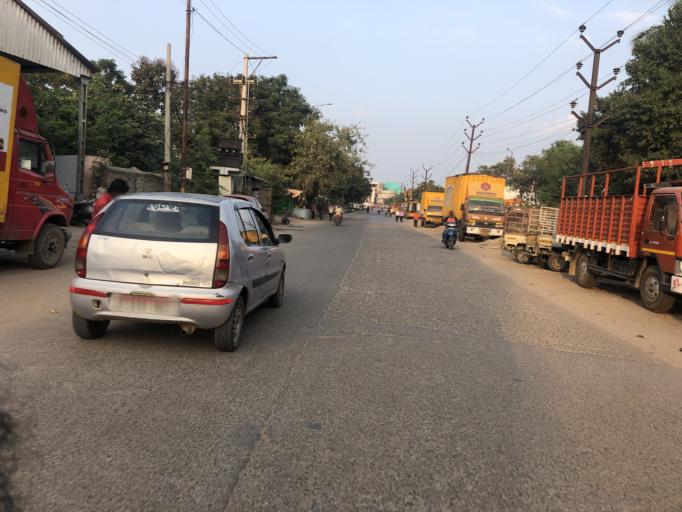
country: IN
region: Telangana
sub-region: Rangareddi
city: Kukatpalli
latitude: 17.4649
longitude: 78.4436
